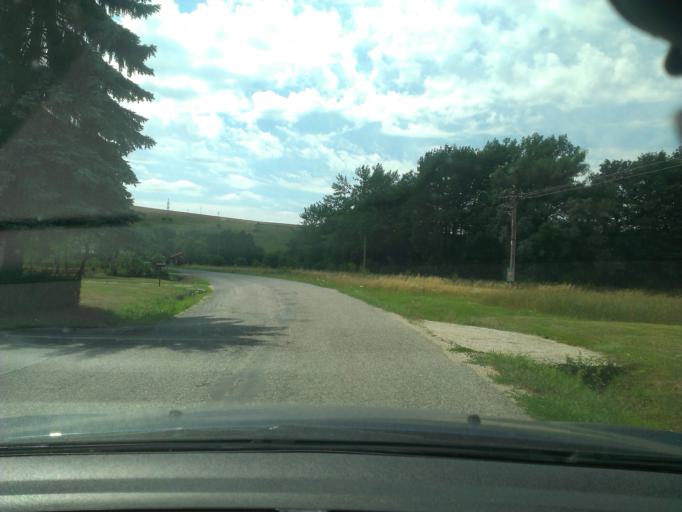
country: SK
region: Trenciansky
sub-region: Okres Myjava
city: Myjava
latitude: 48.7787
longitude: 17.5818
